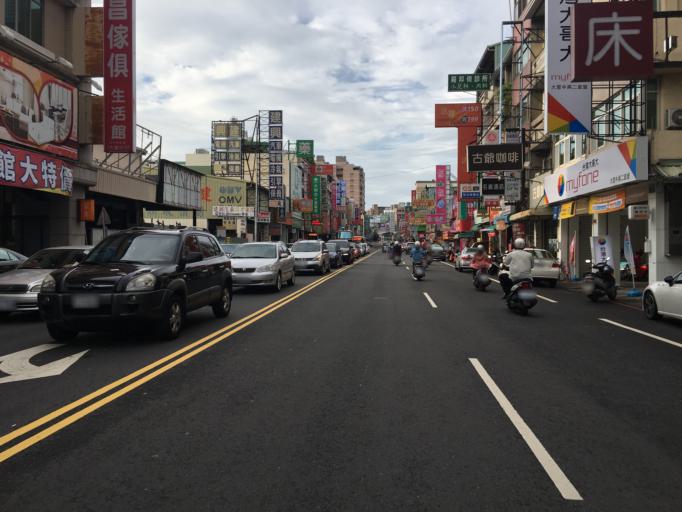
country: TW
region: Taiwan
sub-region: Taichung City
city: Taichung
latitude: 24.1022
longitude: 120.6884
